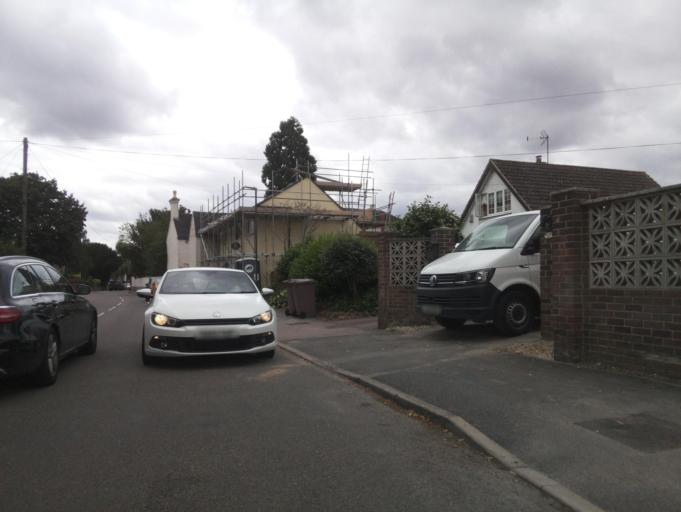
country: GB
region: England
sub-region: Derbyshire
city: Long Eaton
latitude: 52.9001
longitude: -1.3165
